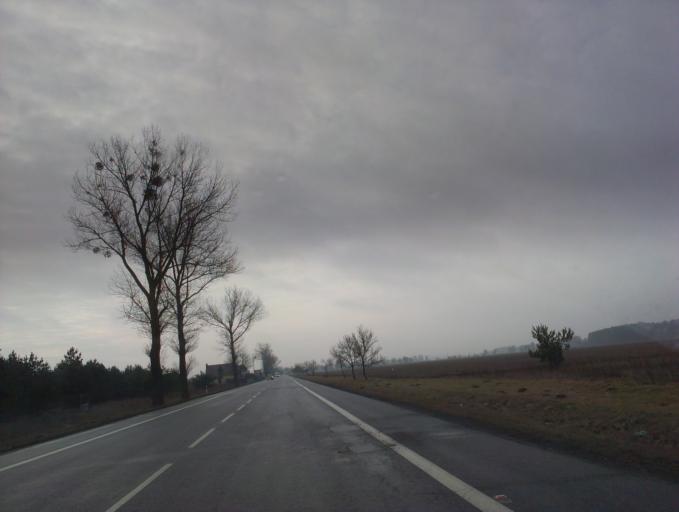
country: PL
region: Greater Poland Voivodeship
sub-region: Powiat pilski
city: Pila
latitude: 53.1080
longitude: 16.7491
